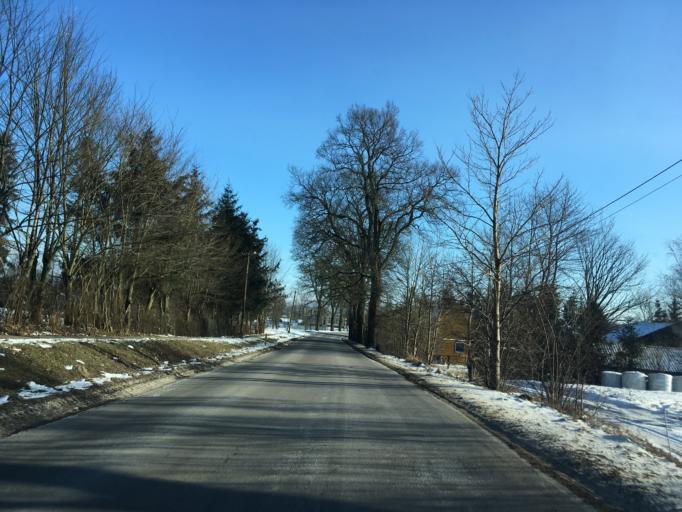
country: PL
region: Pomeranian Voivodeship
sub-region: Powiat koscierski
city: Koscierzyna
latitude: 54.0722
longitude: 18.0078
